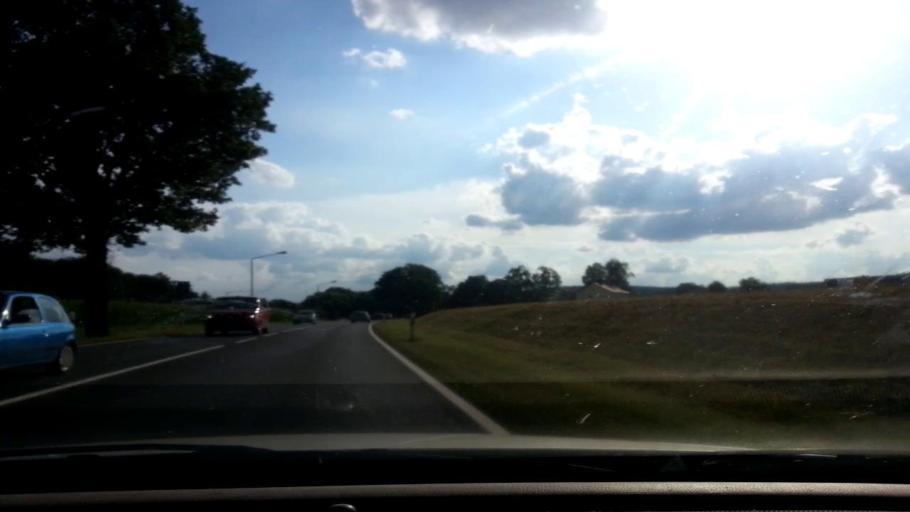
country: DE
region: Bavaria
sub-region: Upper Palatinate
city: Waldsassen
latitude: 49.9933
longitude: 12.2904
